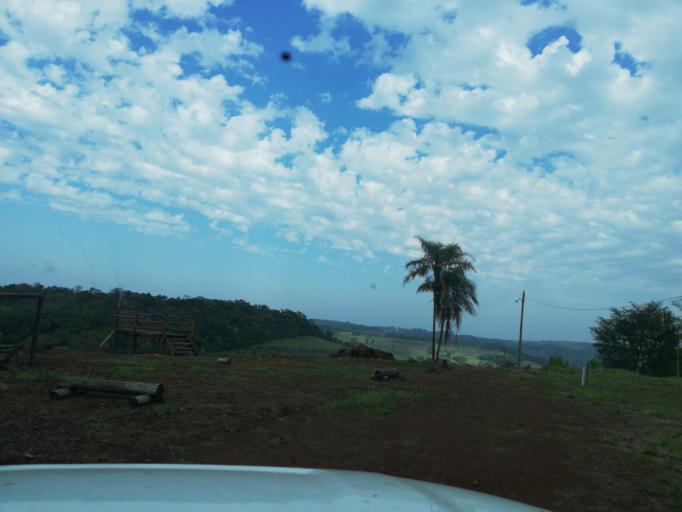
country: AR
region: Misiones
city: Cerro Azul
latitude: -27.6045
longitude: -55.4938
